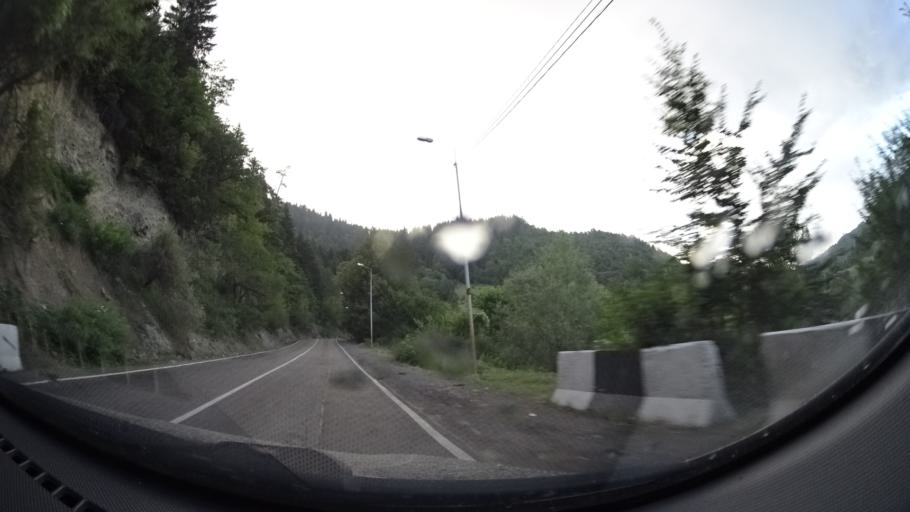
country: GE
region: Samtskhe-Javakheti
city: Borjomi
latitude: 41.8646
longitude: 43.4111
